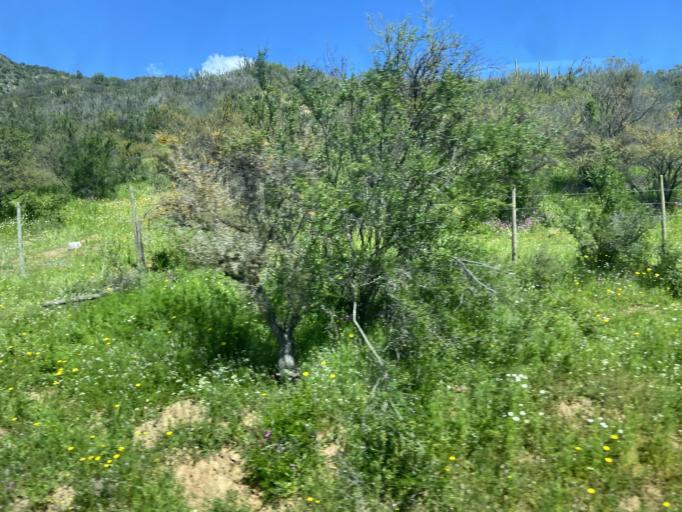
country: CL
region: Valparaiso
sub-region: Provincia de Marga Marga
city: Villa Alemana
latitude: -33.1918
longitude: -71.2845
